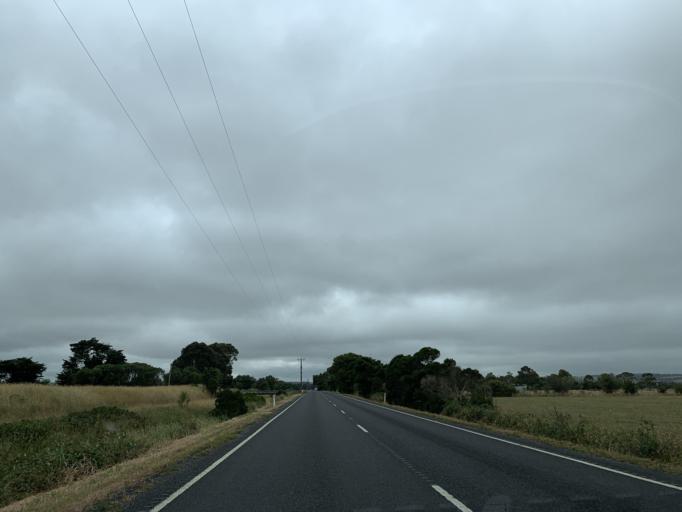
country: AU
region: Victoria
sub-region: Cardinia
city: Bunyip
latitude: -38.1849
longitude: 145.6890
